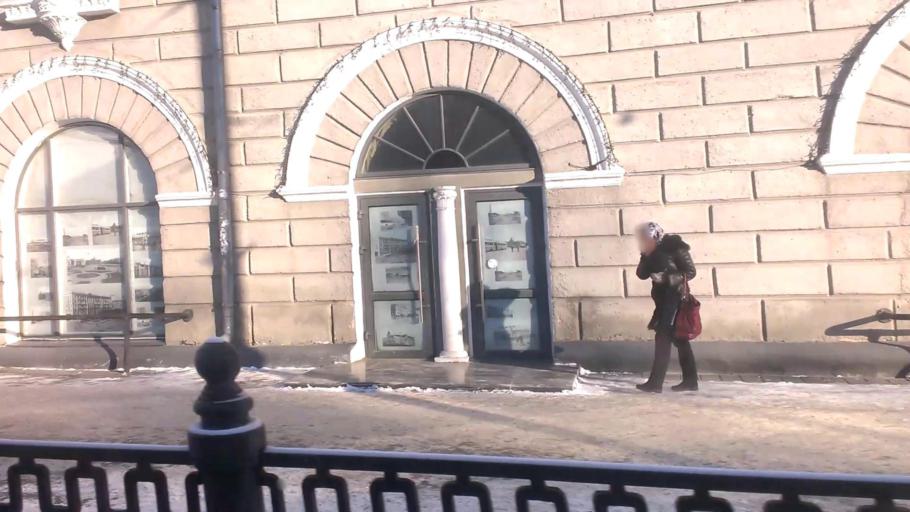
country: RU
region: Altai Krai
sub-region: Gorod Barnaulskiy
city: Barnaul
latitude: 53.3542
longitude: 83.7707
